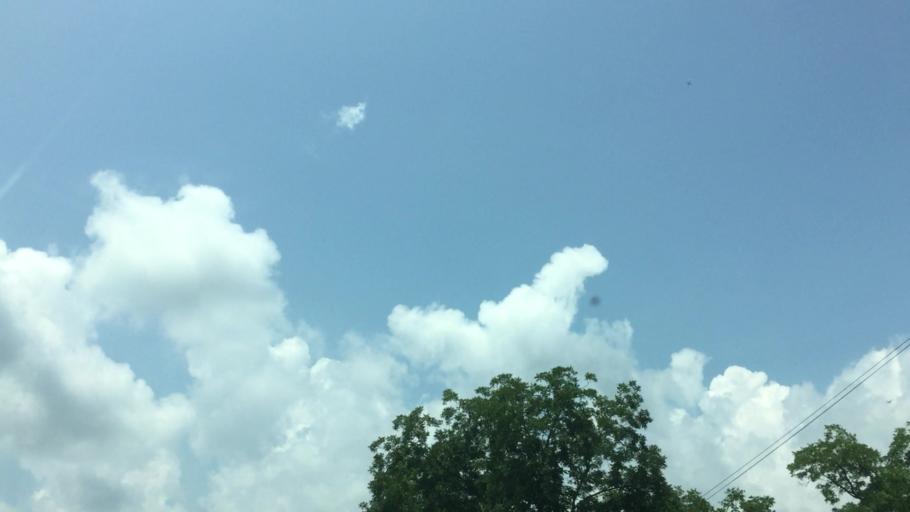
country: US
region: Georgia
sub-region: Fulton County
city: Chattahoochee Hills
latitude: 33.6155
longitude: -84.8406
